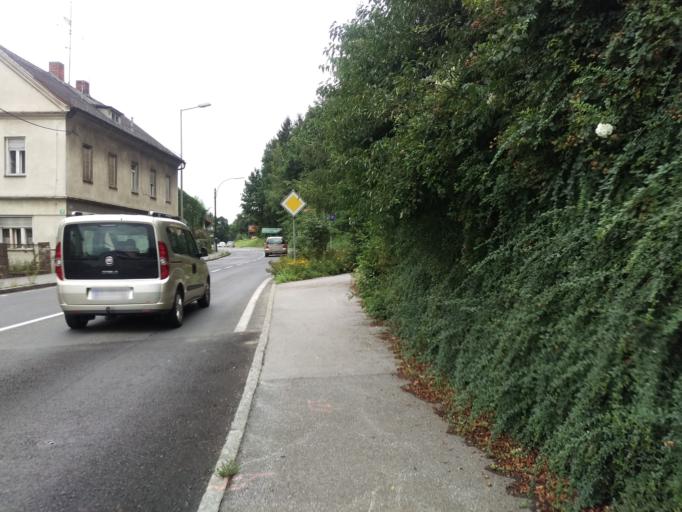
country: AT
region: Styria
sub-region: Politischer Bezirk Graz-Umgebung
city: Raaba
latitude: 47.0357
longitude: 15.4928
